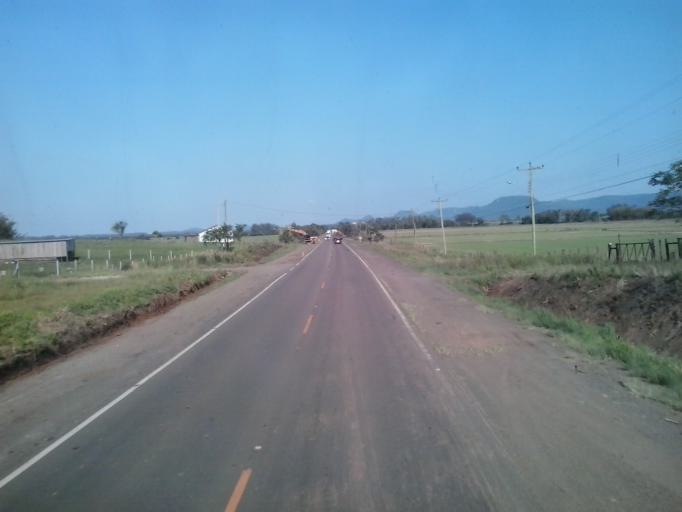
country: BR
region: Rio Grande do Sul
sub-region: Santa Maria
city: Santa Maria
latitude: -29.7185
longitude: -53.6176
